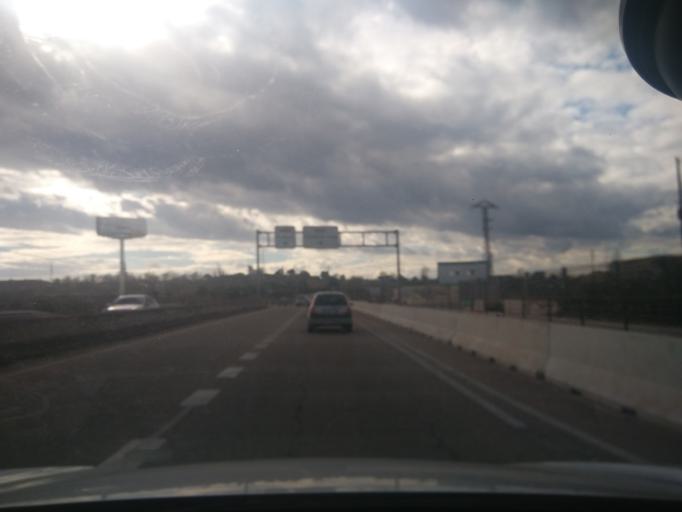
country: ES
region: Madrid
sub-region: Provincia de Madrid
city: Las Tablas
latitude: 40.5489
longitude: -3.7002
